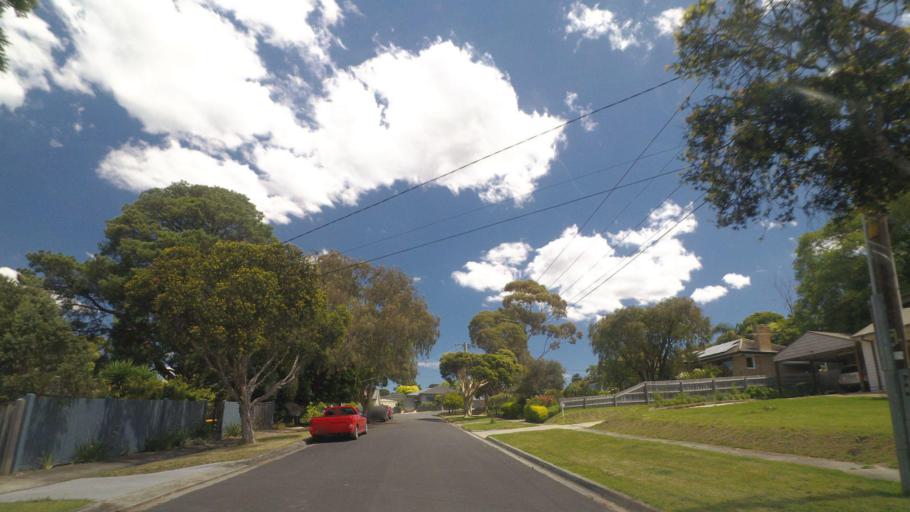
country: AU
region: Victoria
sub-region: Yarra Ranges
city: Kilsyth
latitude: -37.8036
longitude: 145.3225
